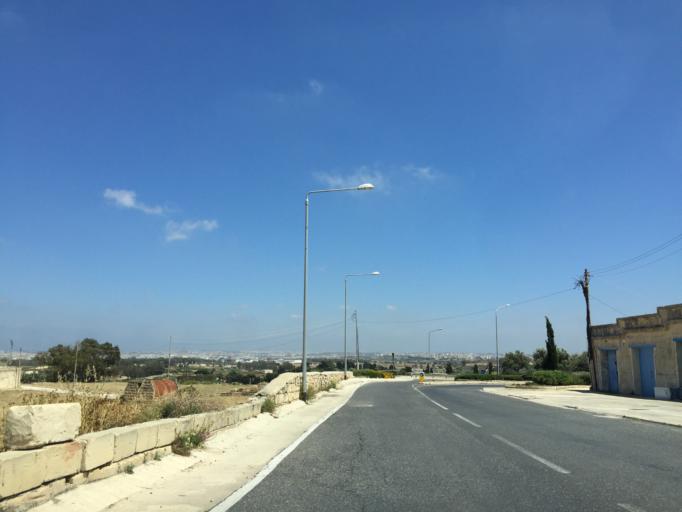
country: MT
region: L-Imtarfa
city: Imtarfa
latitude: 35.8924
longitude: 14.4040
